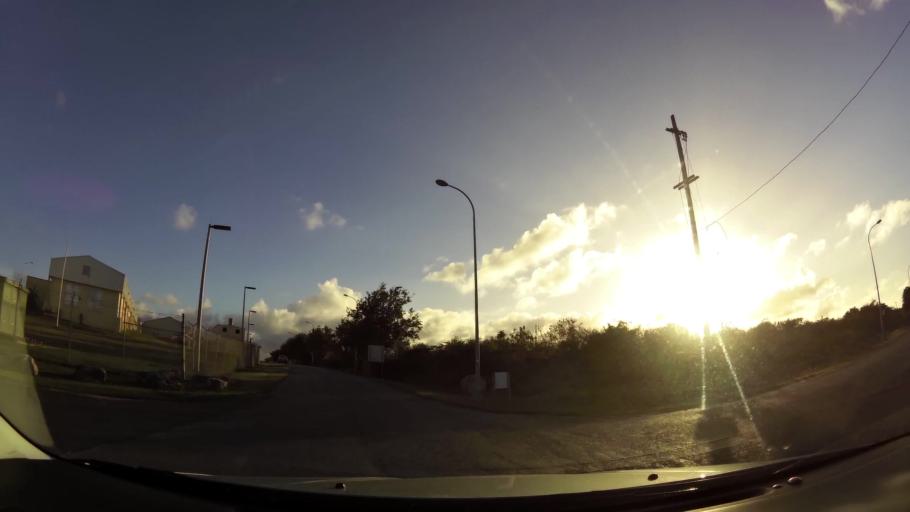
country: AG
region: Saint George
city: Piggotts
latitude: 17.1516
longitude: -61.7943
